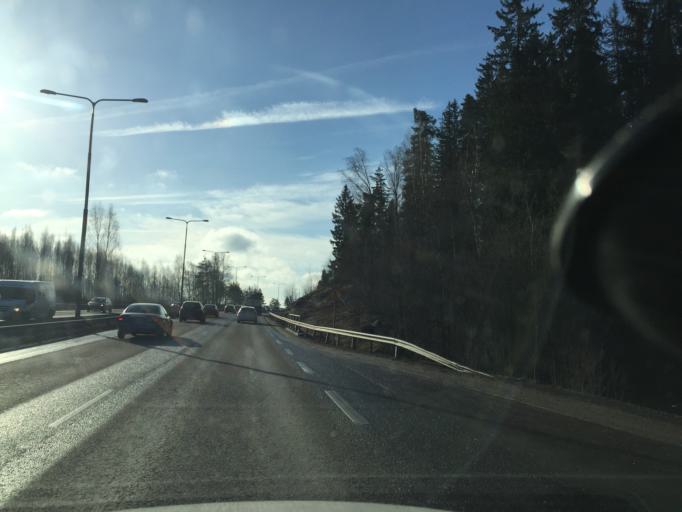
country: FI
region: Uusimaa
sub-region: Helsinki
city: Teekkarikylae
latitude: 60.2739
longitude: 24.8719
